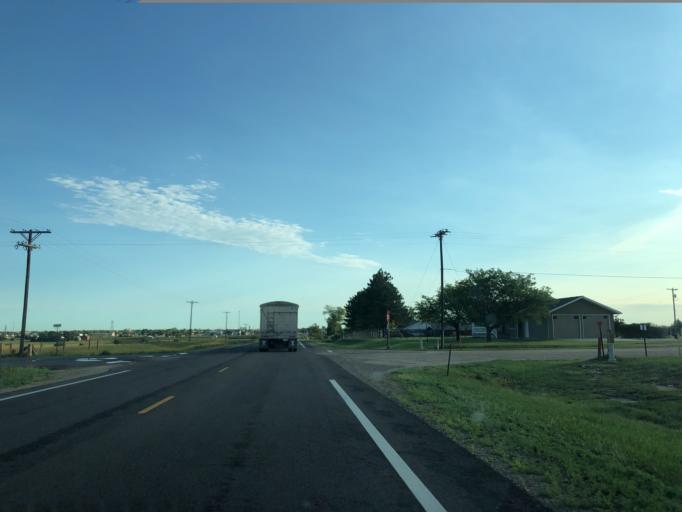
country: US
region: Kansas
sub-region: Russell County
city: Russell
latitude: 38.8558
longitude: -98.8546
